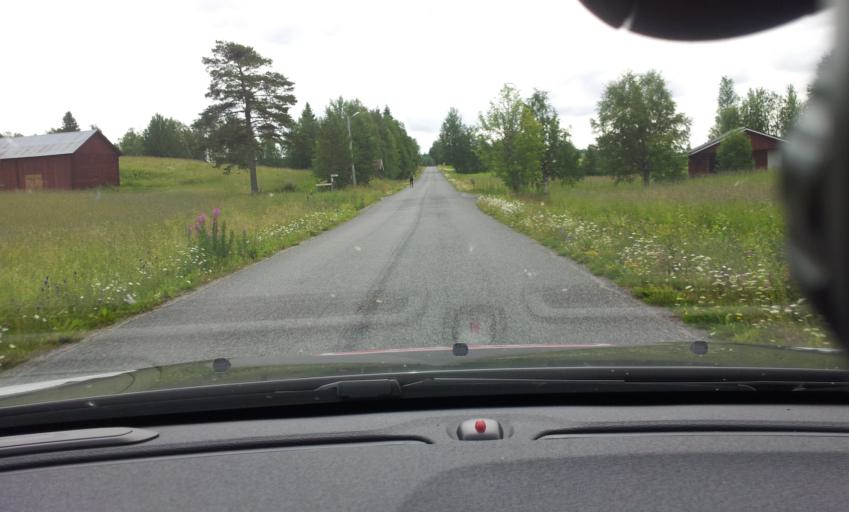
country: SE
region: Jaemtland
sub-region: OEstersunds Kommun
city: Brunflo
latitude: 62.9787
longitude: 14.8941
